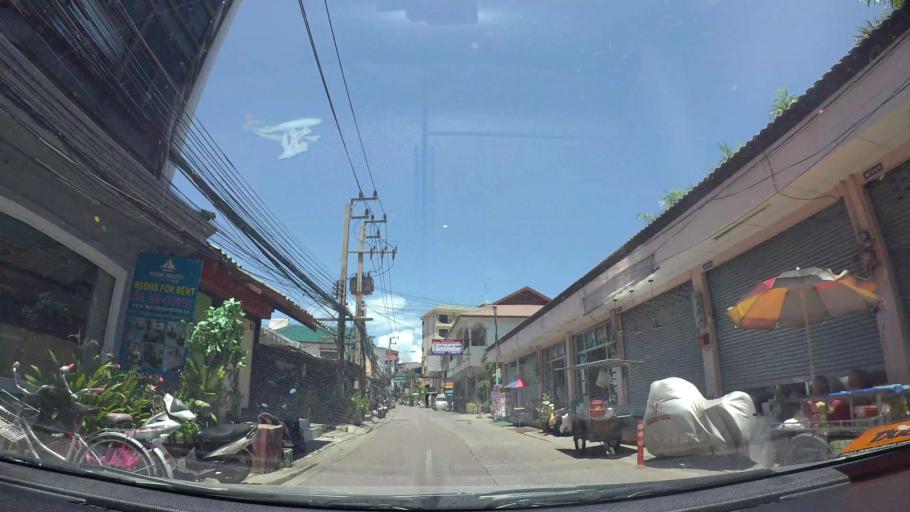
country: TH
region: Chon Buri
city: Phatthaya
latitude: 12.9222
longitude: 100.8747
